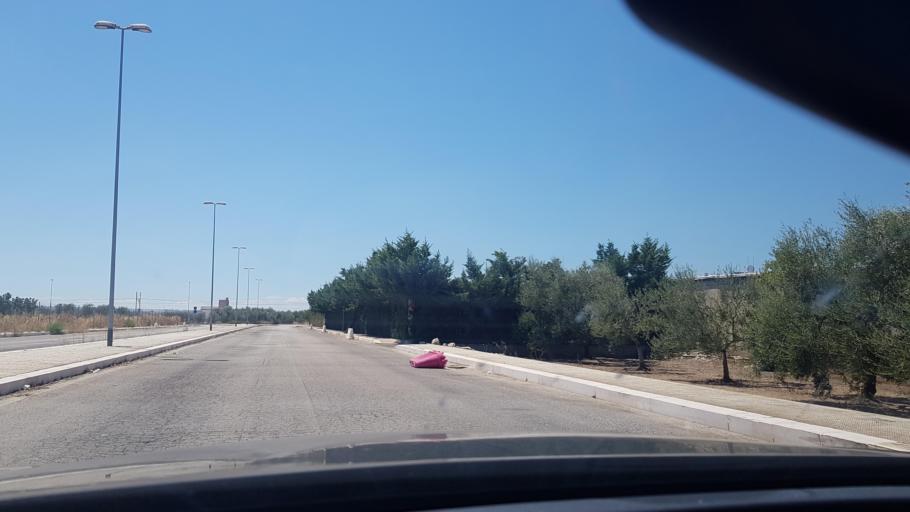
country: IT
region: Apulia
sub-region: Provincia di Barletta - Andria - Trani
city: Barletta
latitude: 41.3027
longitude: 16.3297
